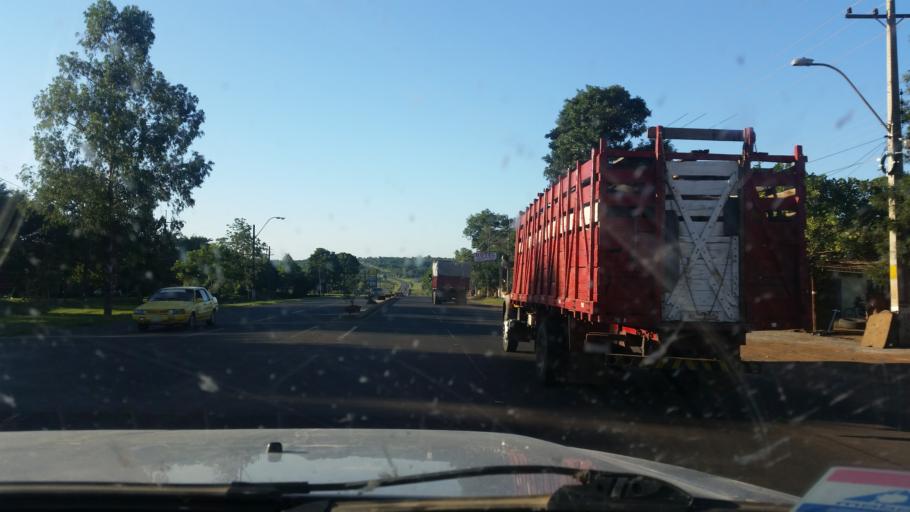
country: PY
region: Misiones
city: Santa Maria
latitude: -26.8768
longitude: -57.0322
